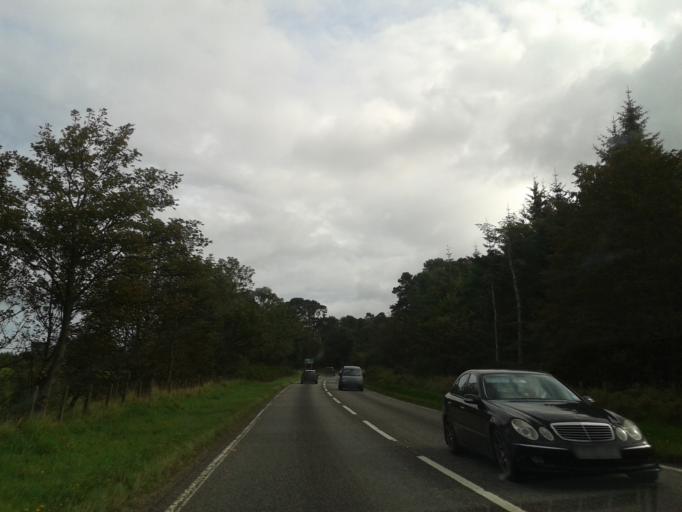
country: GB
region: Scotland
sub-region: Moray
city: Lhanbryd
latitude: 57.6340
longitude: -3.1950
